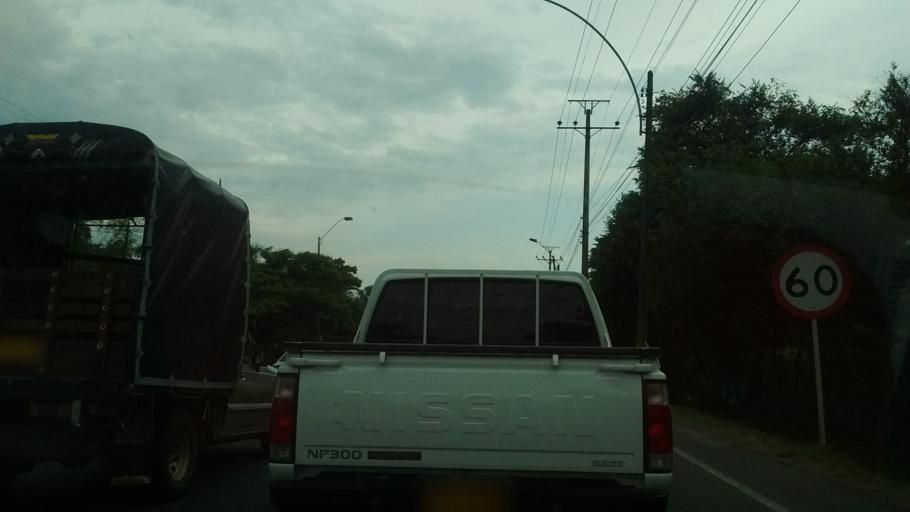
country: CO
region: Valle del Cauca
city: Cali
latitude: 3.3547
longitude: -76.5235
